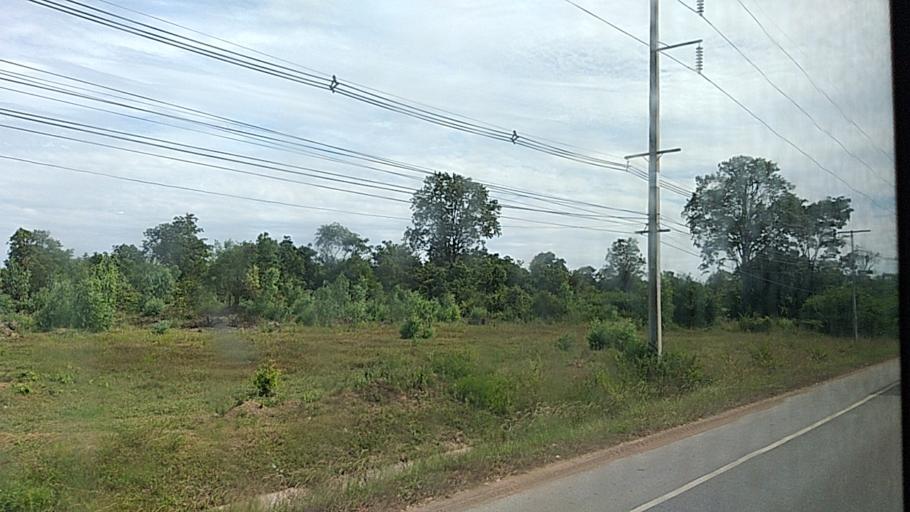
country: TH
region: Maha Sarakham
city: Chiang Yuen
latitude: 16.4438
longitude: 103.0403
